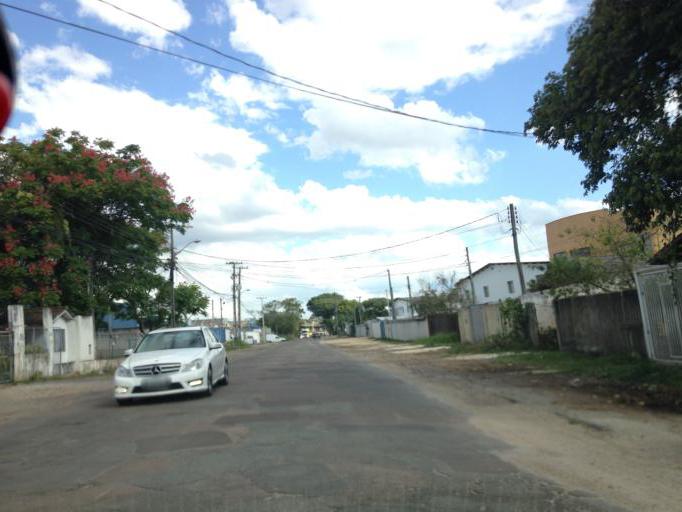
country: BR
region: Parana
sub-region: Pinhais
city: Pinhais
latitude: -25.4151
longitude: -49.2202
